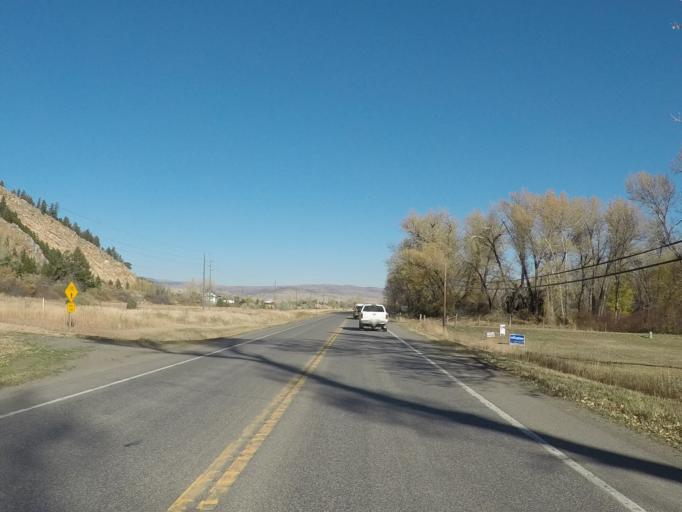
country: US
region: Montana
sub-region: Park County
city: Livingston
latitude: 45.6127
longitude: -110.5777
